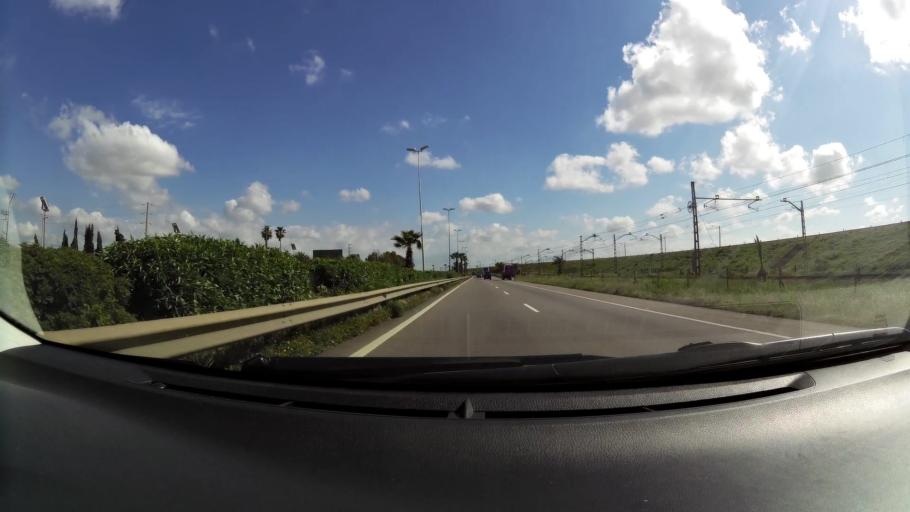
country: MA
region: Chaouia-Ouardigha
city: Nouaseur
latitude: 33.4134
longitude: -7.6265
